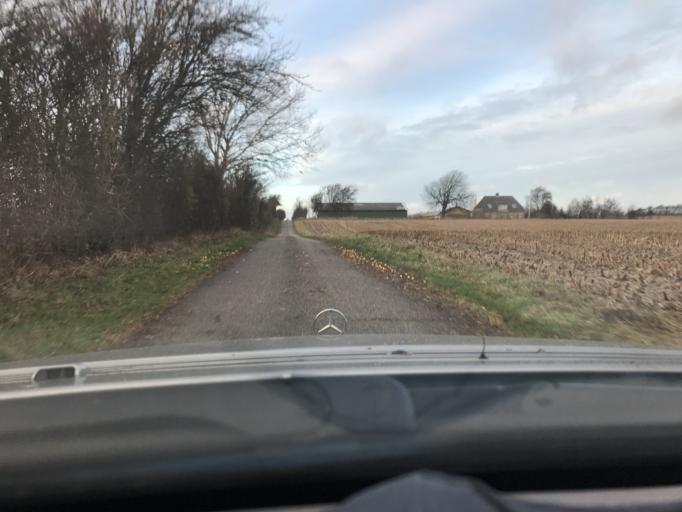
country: DK
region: South Denmark
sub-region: Sonderborg Kommune
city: Nordborg
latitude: 55.0415
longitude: 9.6532
